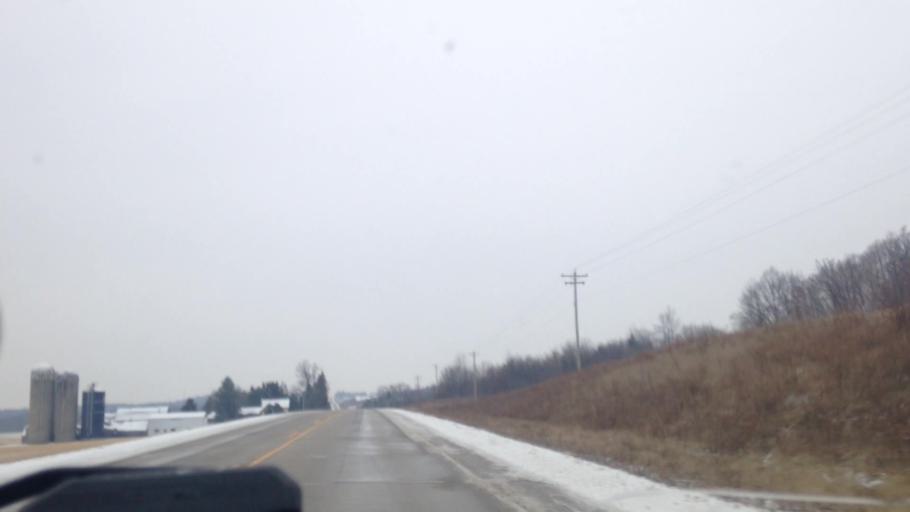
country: US
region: Wisconsin
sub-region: Dodge County
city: Hustisford
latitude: 43.2901
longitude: -88.5186
